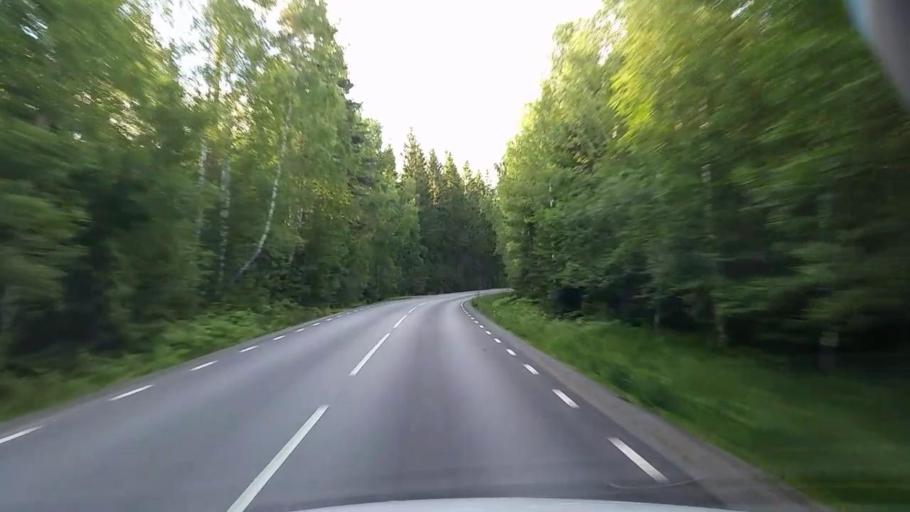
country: SE
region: Vaestmanland
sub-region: Kopings Kommun
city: Kolsva
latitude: 59.6414
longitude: 15.8230
